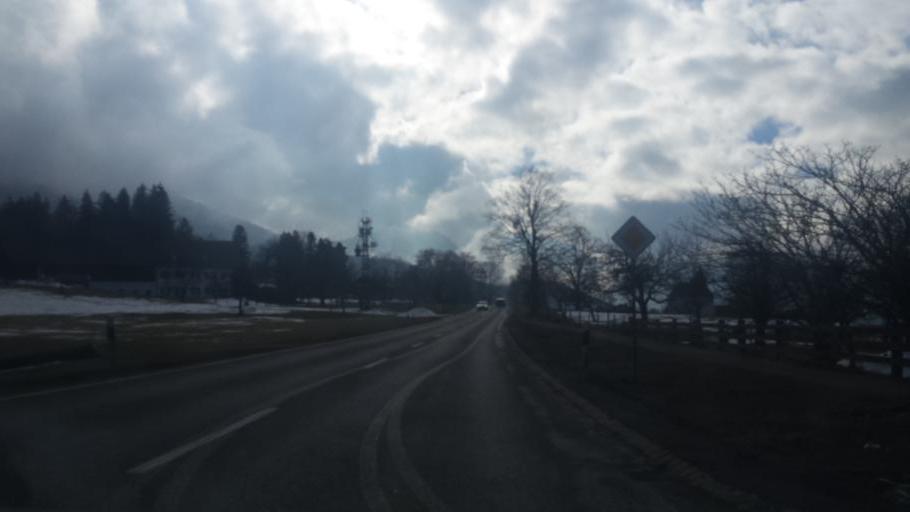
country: DE
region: Bavaria
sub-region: Upper Bavaria
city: Benediktbeuern
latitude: 47.6786
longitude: 11.3999
